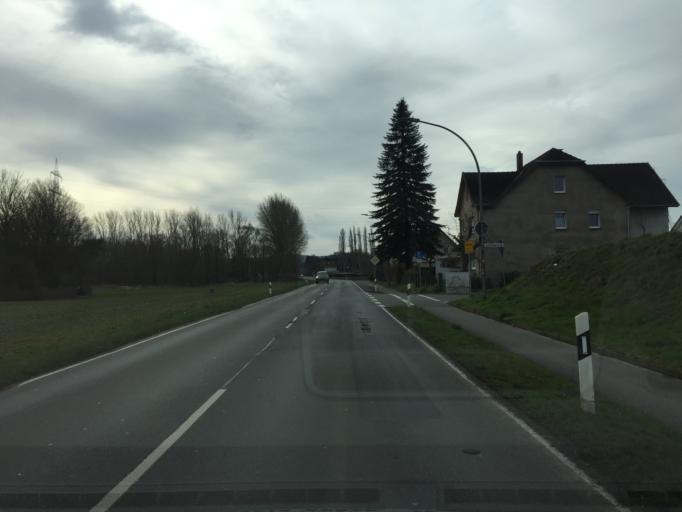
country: DE
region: North Rhine-Westphalia
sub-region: Regierungsbezirk Detmold
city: Lage
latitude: 51.9804
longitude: 8.7978
